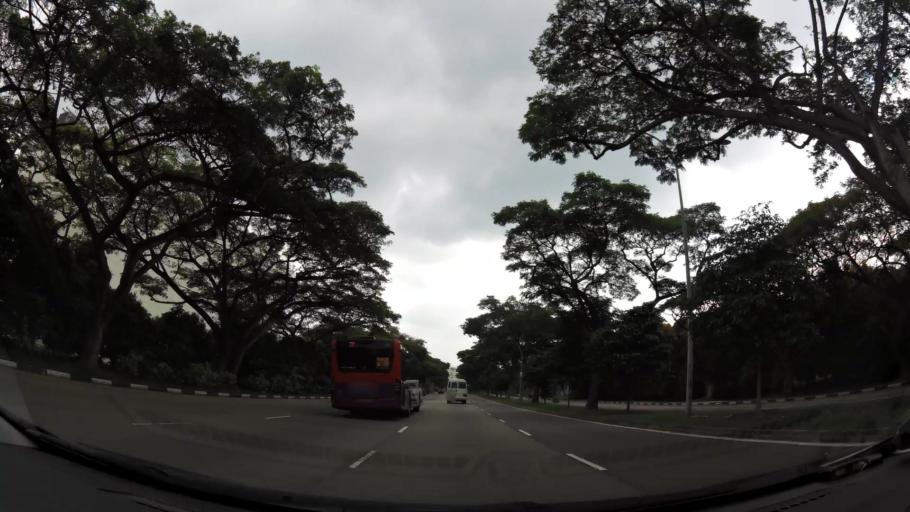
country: SG
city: Singapore
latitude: 1.3435
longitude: 103.9453
